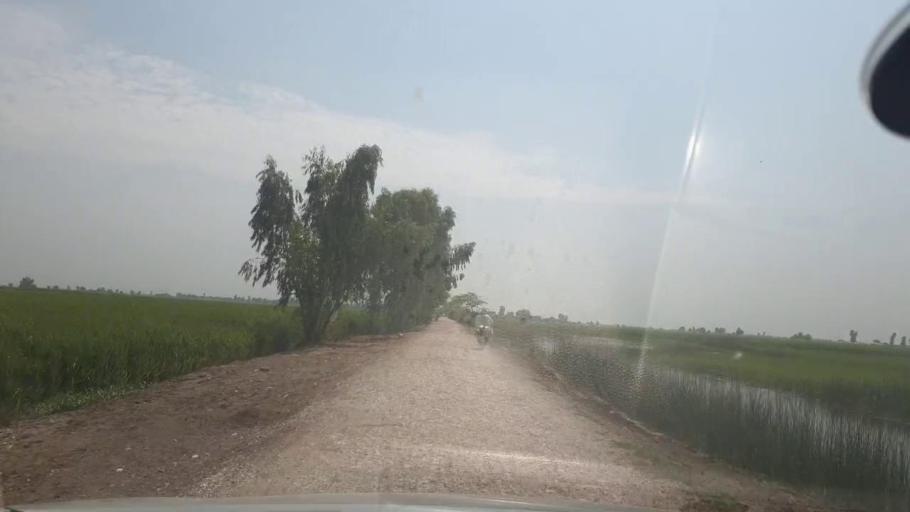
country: PK
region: Sindh
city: Thul
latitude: 28.1668
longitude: 68.6491
